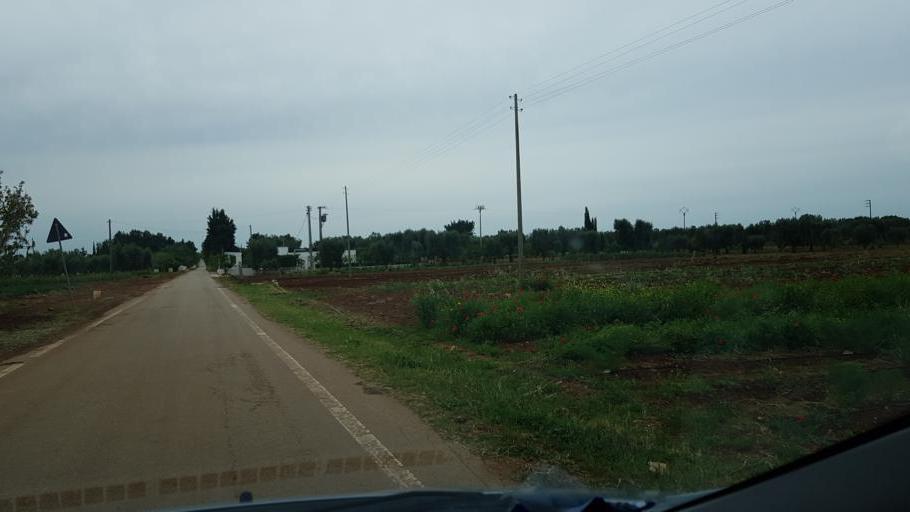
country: IT
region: Apulia
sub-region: Provincia di Brindisi
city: San Vito dei Normanni
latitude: 40.6656
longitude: 17.7750
